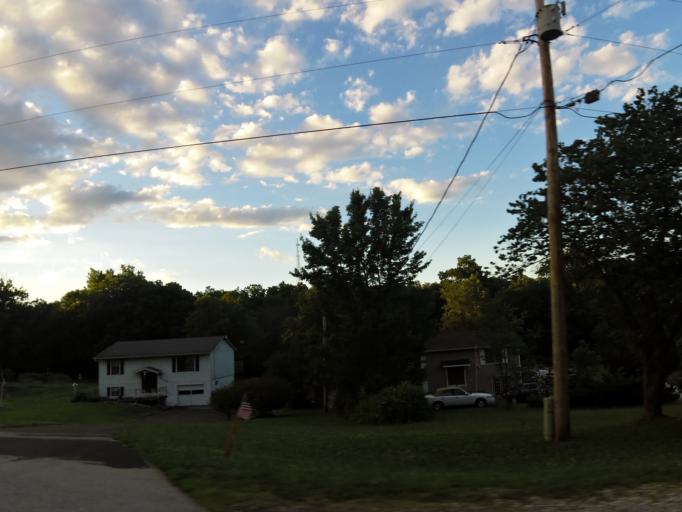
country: US
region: Missouri
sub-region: Jefferson County
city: Cedar Hill
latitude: 38.3349
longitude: -90.6749
